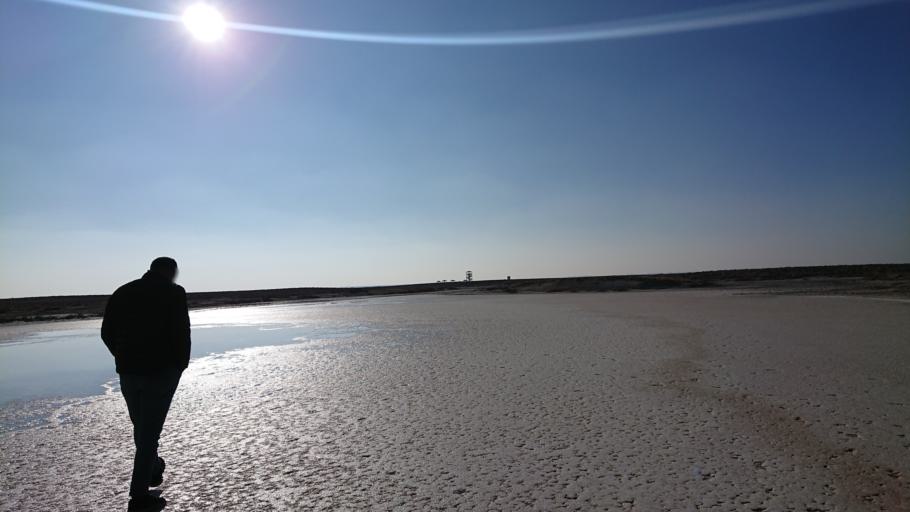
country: TR
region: Aksaray
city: Eskil
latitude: 38.4282
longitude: 33.5062
